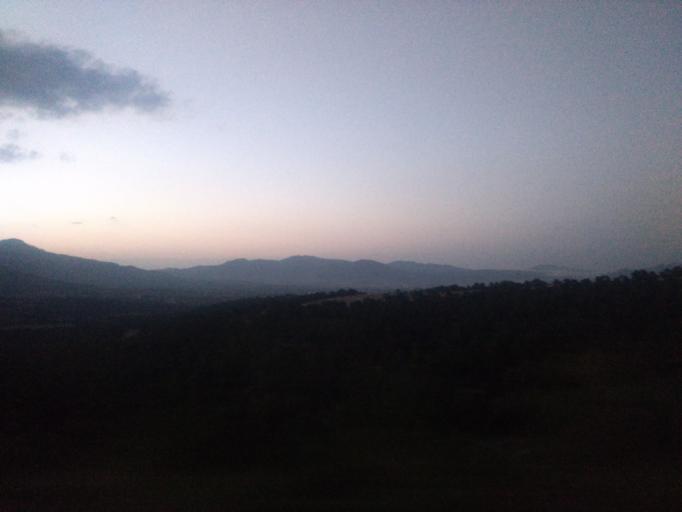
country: MX
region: Puebla
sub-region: Oriental
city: San Antonio Virreyes
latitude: 19.3952
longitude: -97.6840
